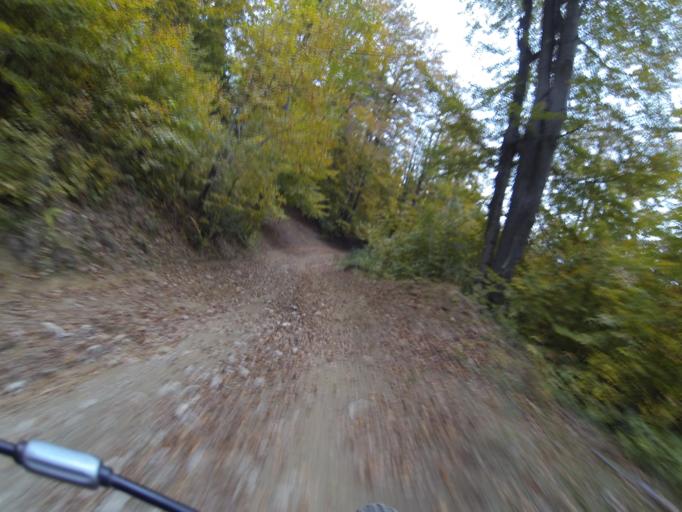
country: RO
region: Gorj
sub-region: Comuna Tismana
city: Sohodol
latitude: 45.1322
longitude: 22.8799
